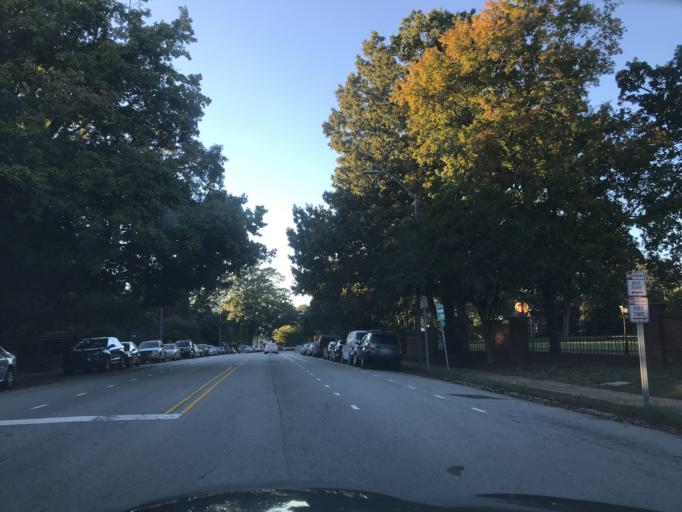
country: US
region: North Carolina
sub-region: Wake County
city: West Raleigh
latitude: 35.7817
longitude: -78.6534
